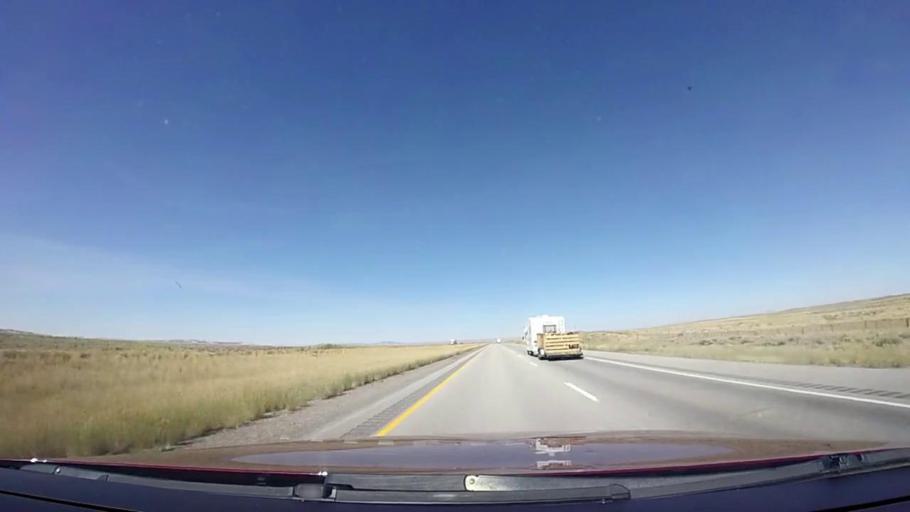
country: US
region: Wyoming
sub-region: Sweetwater County
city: Rock Springs
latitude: 41.6315
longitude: -108.3392
